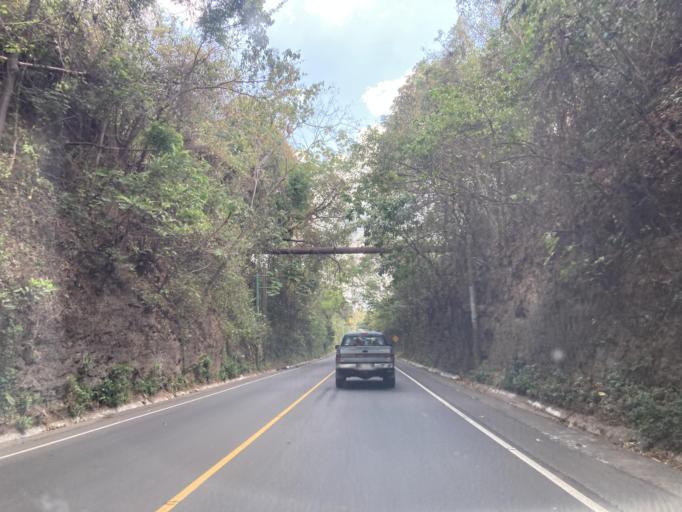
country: GT
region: Santa Rosa
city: Guazacapan
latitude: 14.0713
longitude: -90.4228
